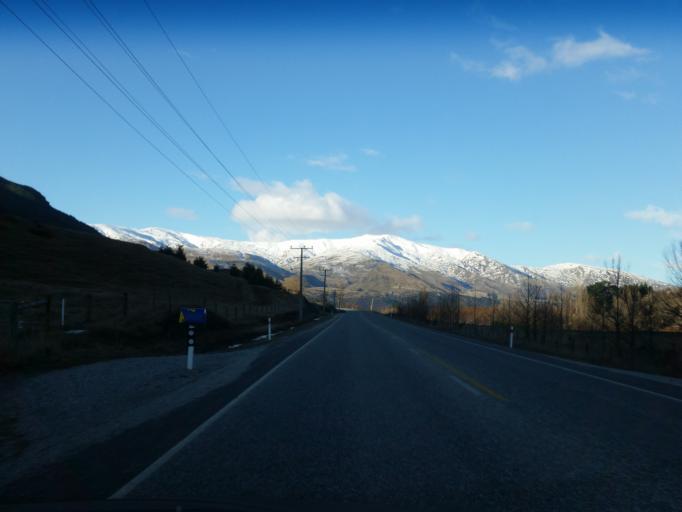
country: NZ
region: Otago
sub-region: Queenstown-Lakes District
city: Arrowtown
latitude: -44.9467
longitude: 168.7797
